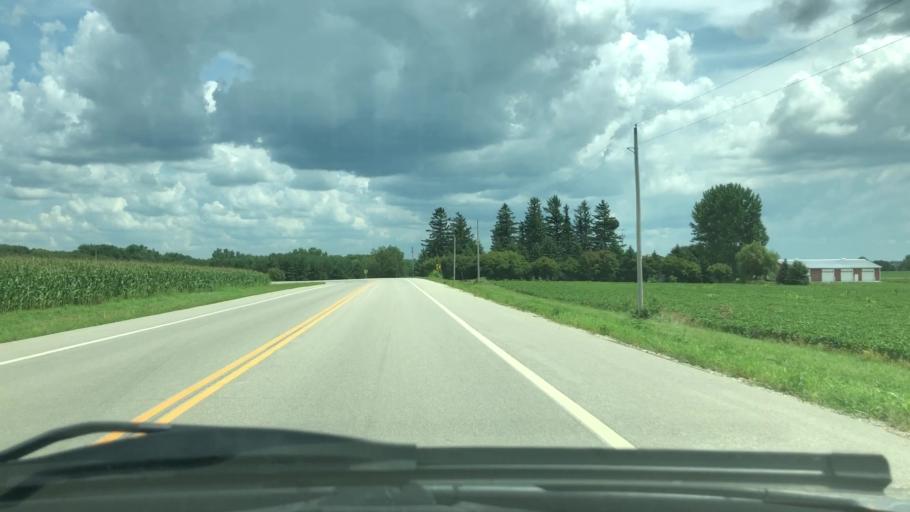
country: US
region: Minnesota
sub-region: Olmsted County
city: Rochester
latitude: 43.9494
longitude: -92.5218
